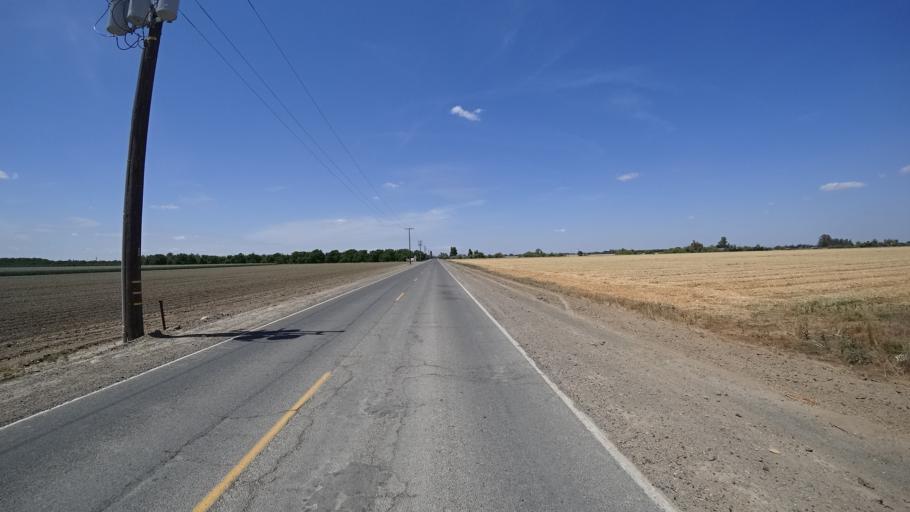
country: US
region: California
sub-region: Kings County
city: Armona
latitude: 36.2984
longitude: -119.6794
